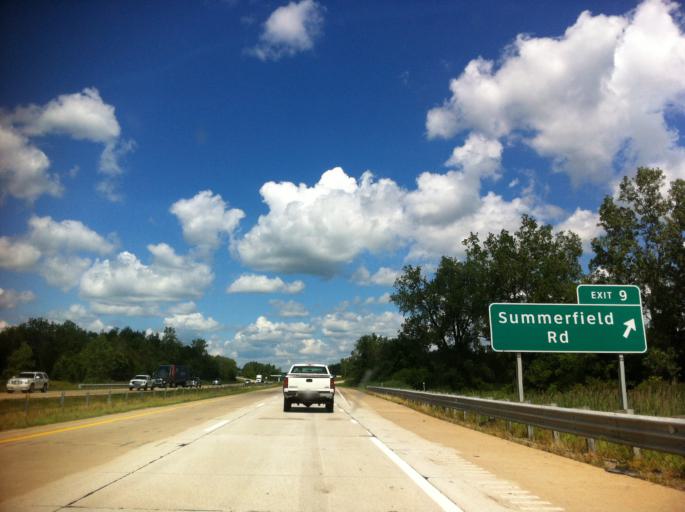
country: US
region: Michigan
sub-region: Monroe County
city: Petersburg
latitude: 41.8365
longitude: -83.6743
